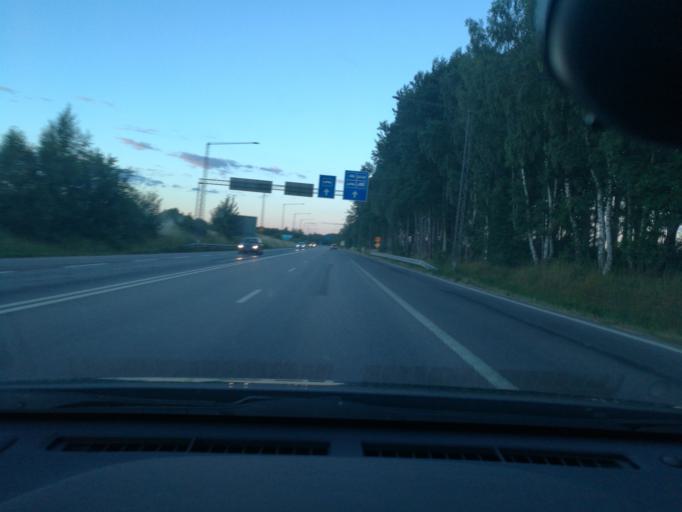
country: SE
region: Kalmar
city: Faerjestaden
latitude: 56.6668
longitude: 16.4899
